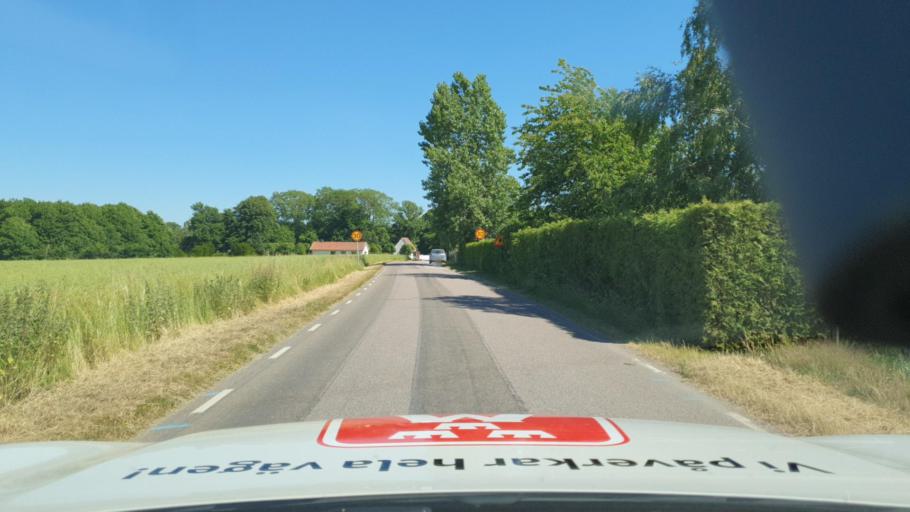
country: SE
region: Skane
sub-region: Eslovs Kommun
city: Eslov
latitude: 55.7881
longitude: 13.2390
